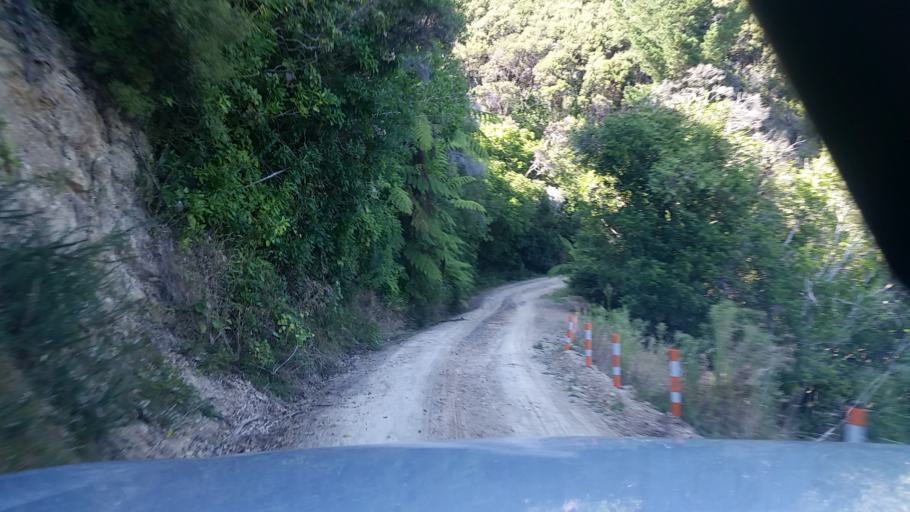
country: NZ
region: Marlborough
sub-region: Marlborough District
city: Picton
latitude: -41.3066
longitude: 174.1734
